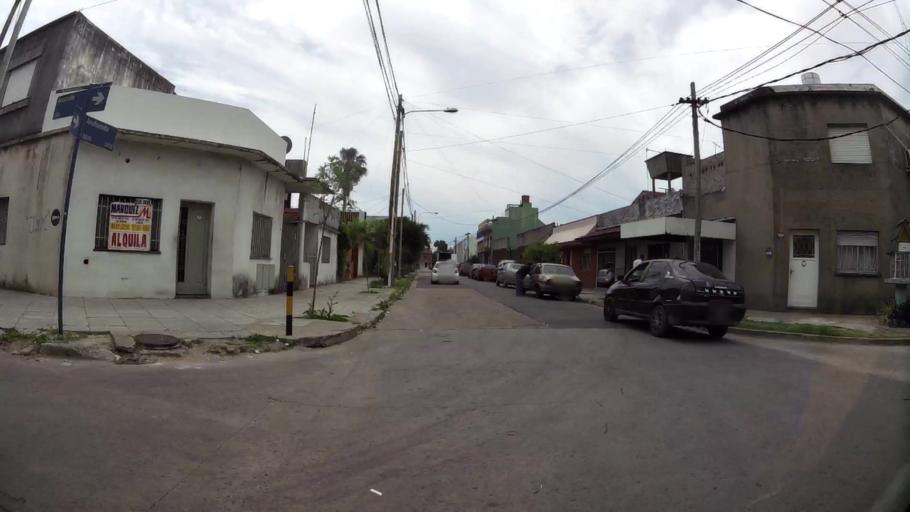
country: AR
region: Buenos Aires
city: San Justo
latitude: -34.6734
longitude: -58.5383
